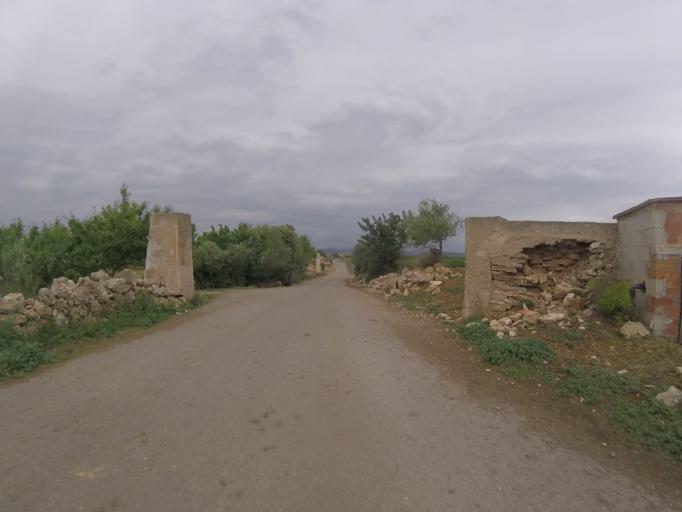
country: ES
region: Valencia
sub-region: Provincia de Castello
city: Torreblanca
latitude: 40.2133
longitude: 0.2418
